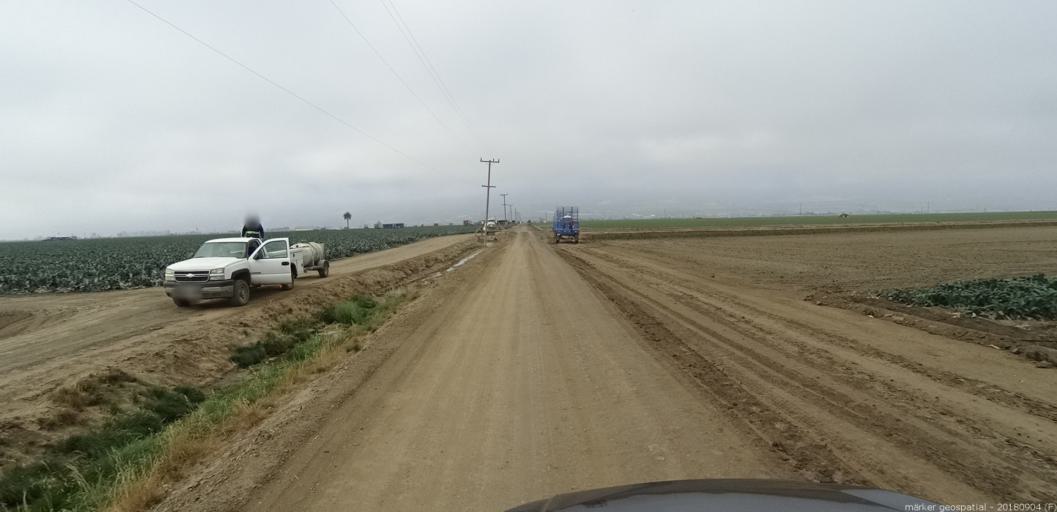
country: US
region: California
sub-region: Monterey County
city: Soledad
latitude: 36.4573
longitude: -121.3798
